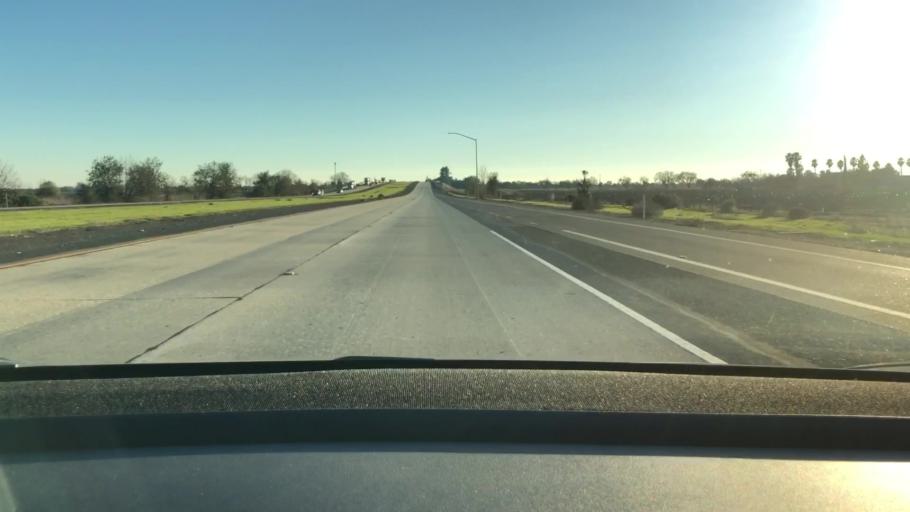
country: US
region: California
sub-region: Yolo County
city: Woodland
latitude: 38.6372
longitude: -121.7617
